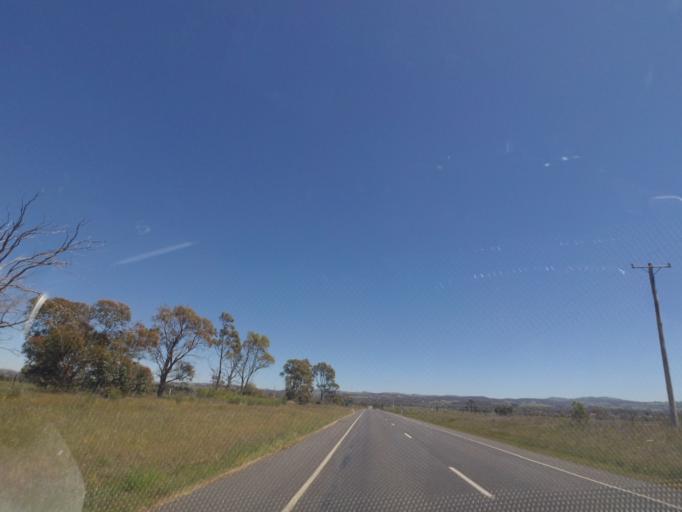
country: AU
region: Victoria
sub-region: Hume
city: Craigieburn
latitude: -37.2895
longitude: 144.8935
